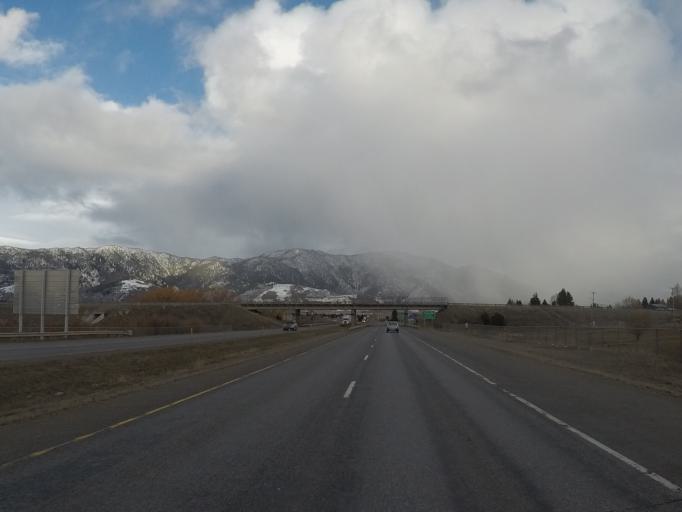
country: US
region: Montana
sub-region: Silver Bow County
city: Butte
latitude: 45.9890
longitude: -112.5231
